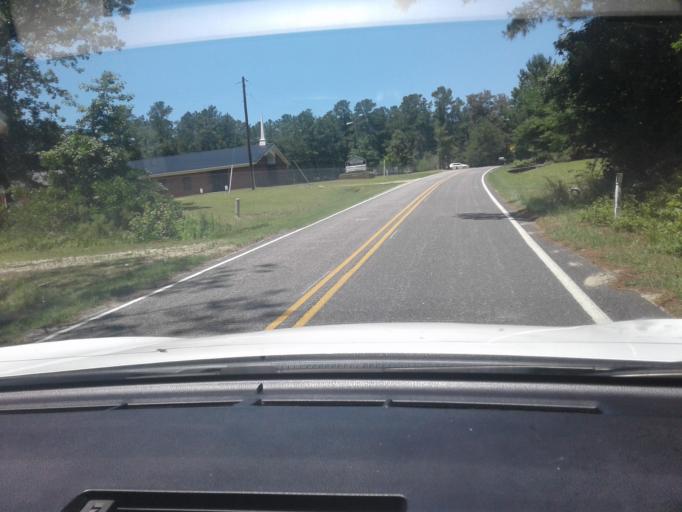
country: US
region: North Carolina
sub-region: Harnett County
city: Lillington
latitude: 35.3503
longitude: -78.9110
